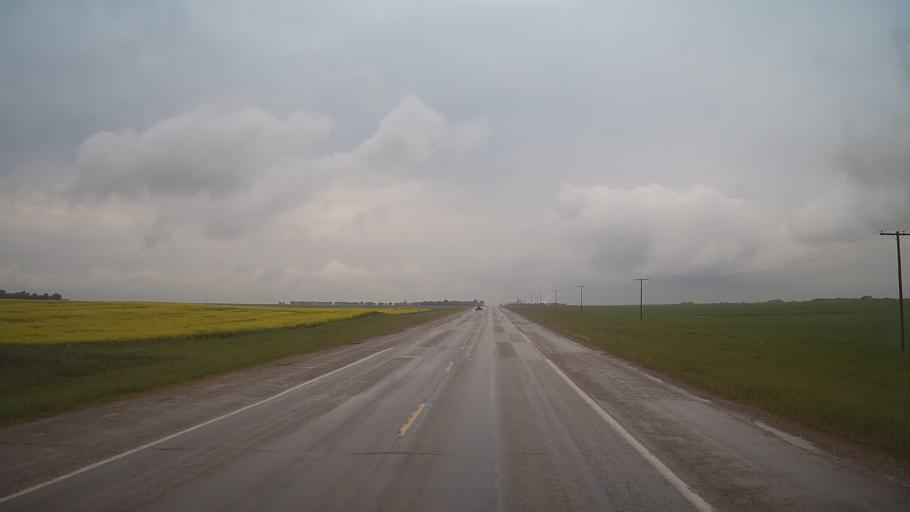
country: CA
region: Saskatchewan
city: Unity
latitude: 52.4350
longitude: -109.0564
